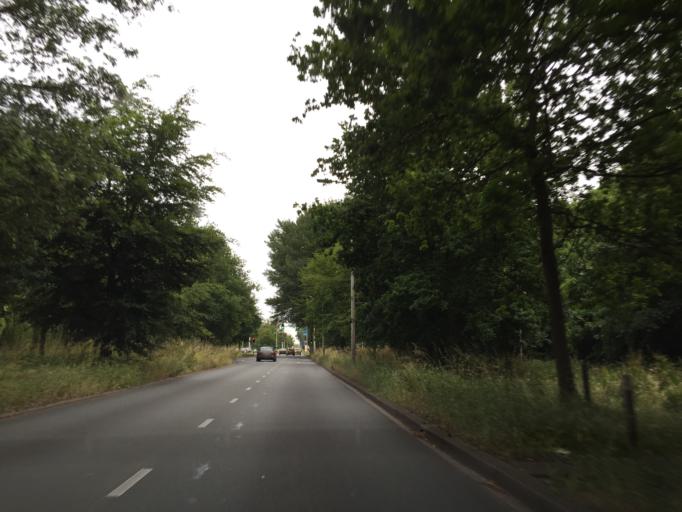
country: NL
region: South Holland
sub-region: Gemeente Westland
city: Kwintsheul
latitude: 52.0347
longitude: 4.2543
